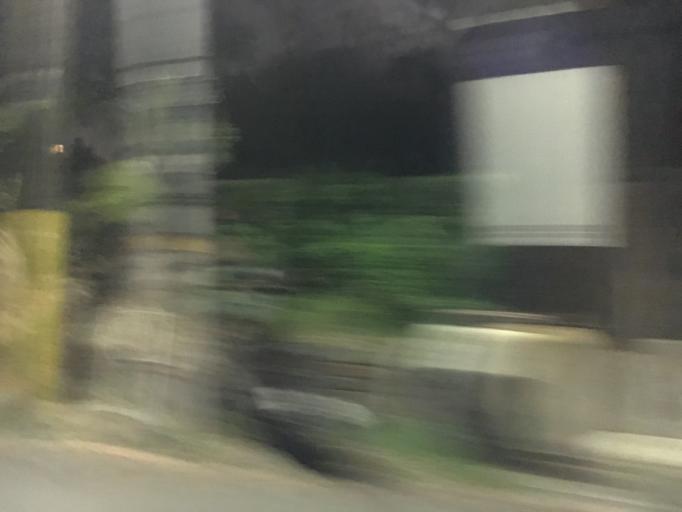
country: TW
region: Taiwan
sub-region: Hsinchu
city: Hsinchu
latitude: 24.7818
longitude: 120.9669
